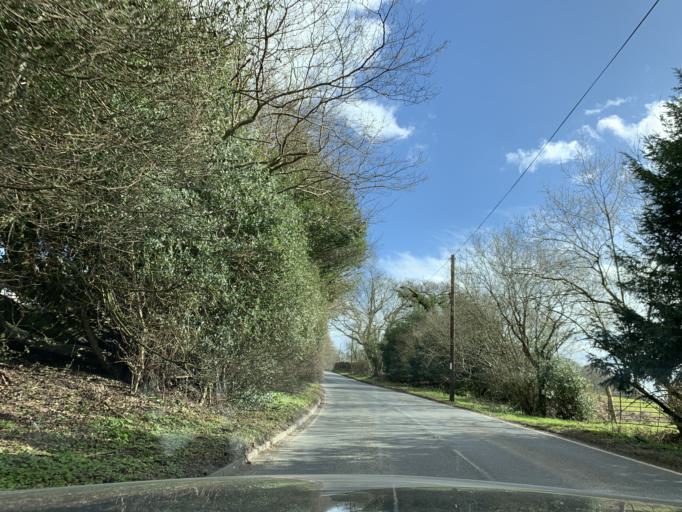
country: GB
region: England
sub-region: West Sussex
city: Crawley Down
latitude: 51.0934
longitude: -0.0785
